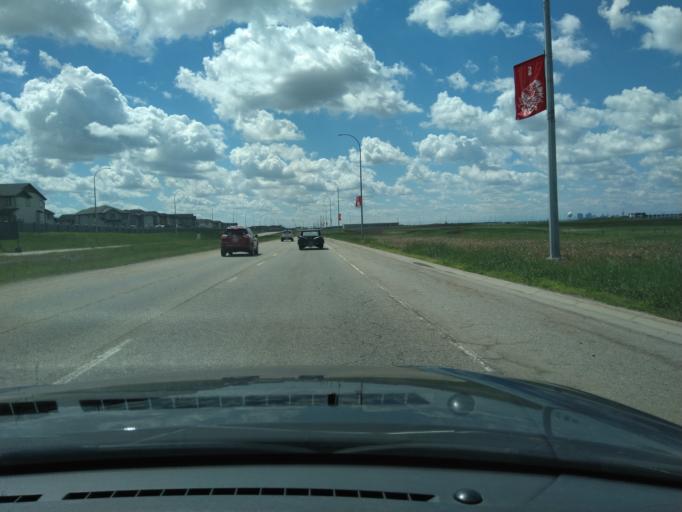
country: CA
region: Alberta
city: Airdrie
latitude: 51.1608
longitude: -113.9702
